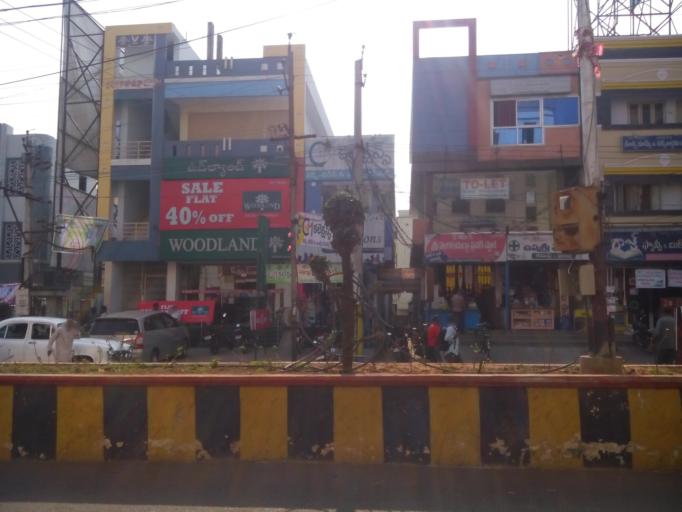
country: IN
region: Andhra Pradesh
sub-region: East Godavari
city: Rajahmundry
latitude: 16.9957
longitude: 81.7745
